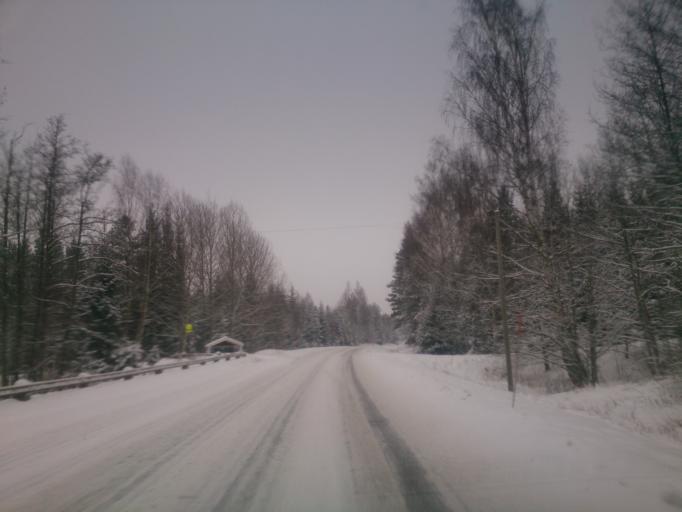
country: SE
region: OEstergoetland
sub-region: Norrkopings Kommun
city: Skarblacka
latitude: 58.6113
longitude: 15.8119
